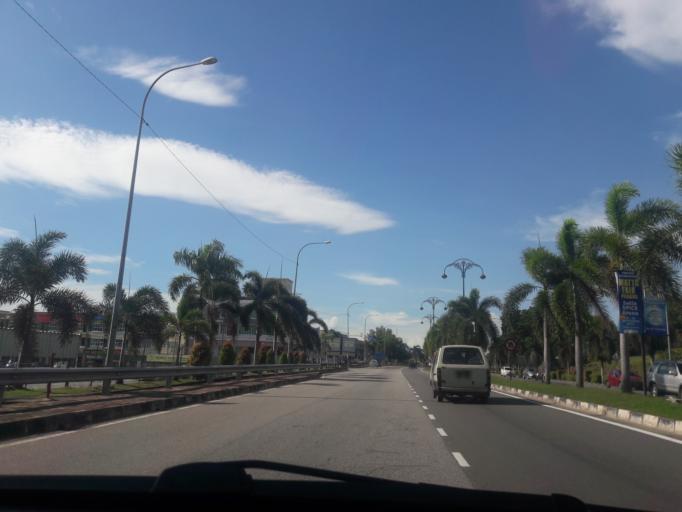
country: MY
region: Kedah
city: Sungai Petani
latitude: 5.6158
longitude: 100.4729
